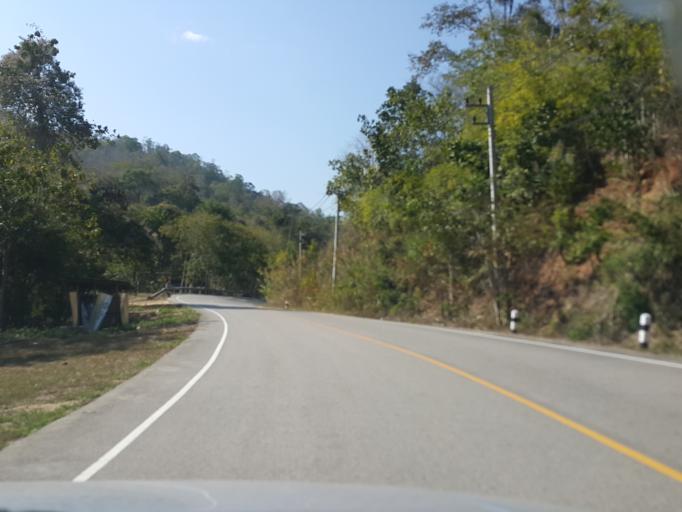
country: TH
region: Chiang Mai
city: Mae Wang
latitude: 18.6256
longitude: 98.7155
